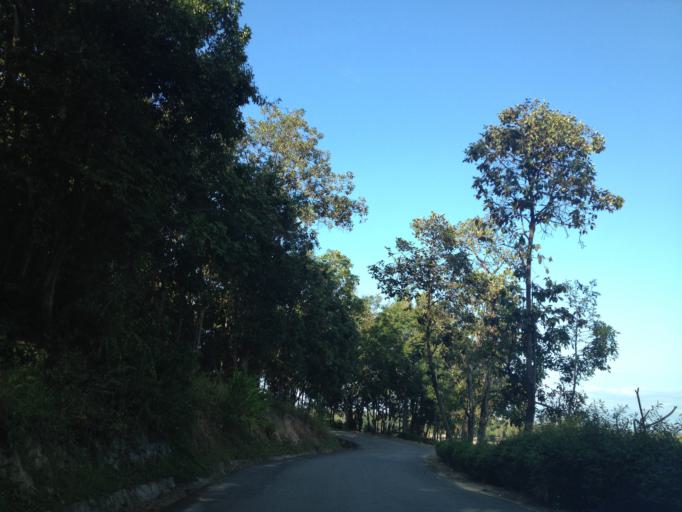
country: TH
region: Chiang Mai
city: Chiang Mai
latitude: 18.8635
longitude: 98.9395
